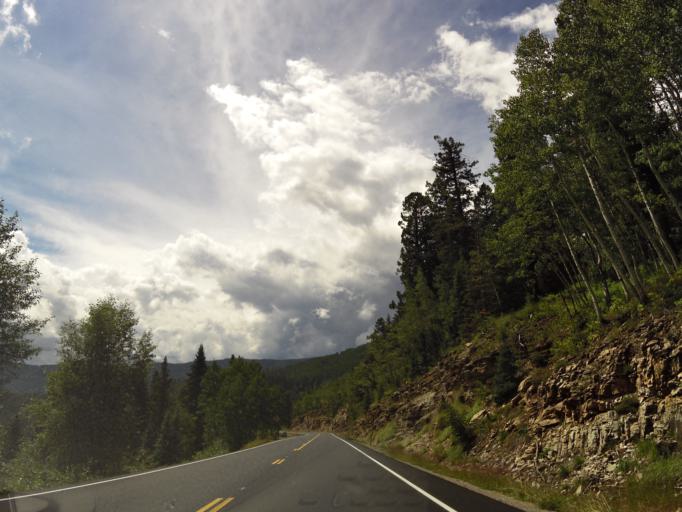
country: US
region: Colorado
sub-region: San Juan County
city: Silverton
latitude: 37.6803
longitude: -107.7894
